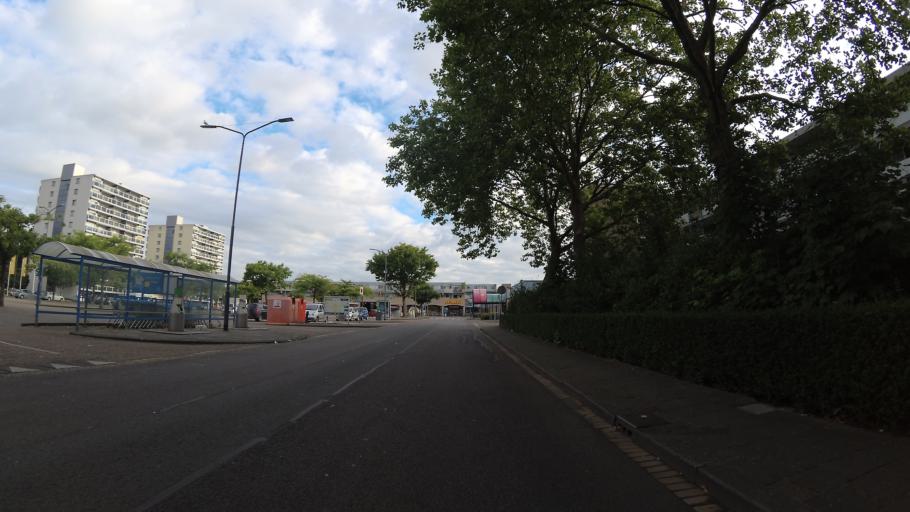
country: NL
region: North Brabant
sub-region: Gemeente Breda
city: Hoge Vucht
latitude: 51.6074
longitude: 4.7891
